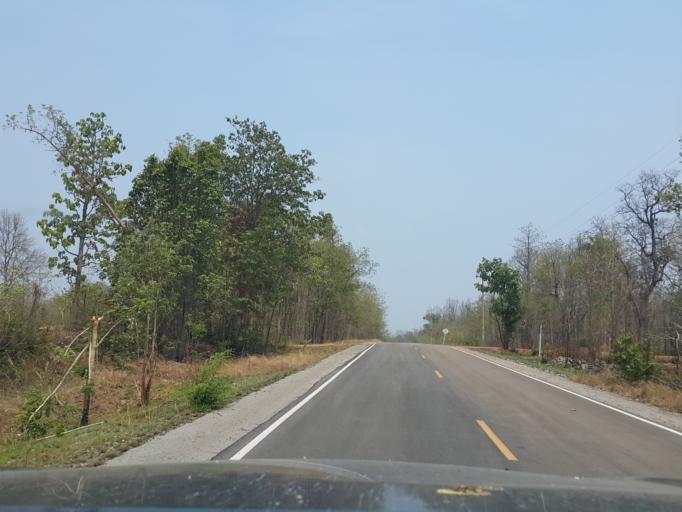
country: TH
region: Lampang
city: Mae Phrik
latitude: 17.5583
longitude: 99.1011
